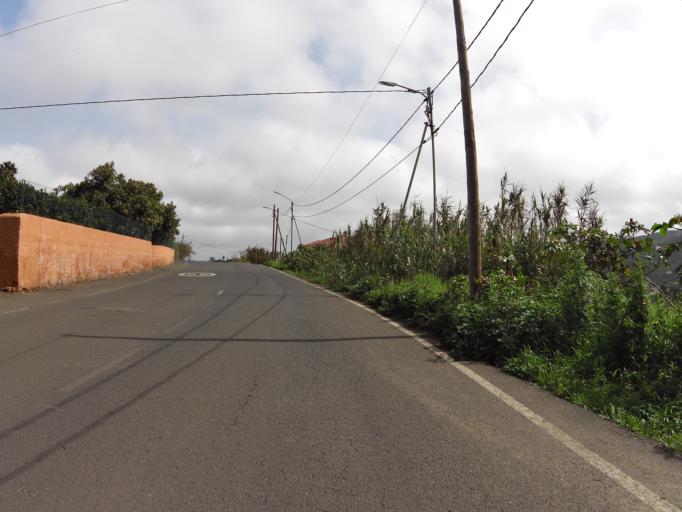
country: ES
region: Canary Islands
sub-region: Provincia de Las Palmas
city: Teror
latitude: 28.0631
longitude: -15.5428
